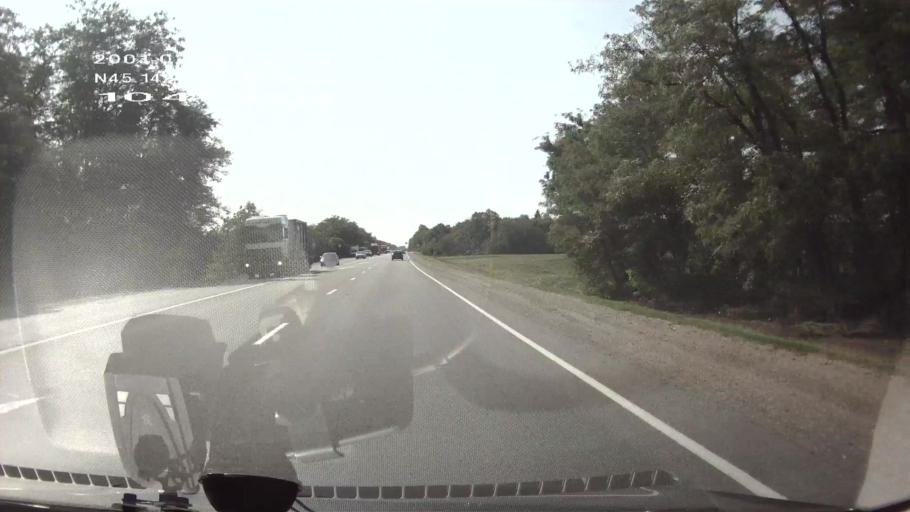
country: RU
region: Krasnodarskiy
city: Vasyurinskaya
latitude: 45.1423
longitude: 39.4278
